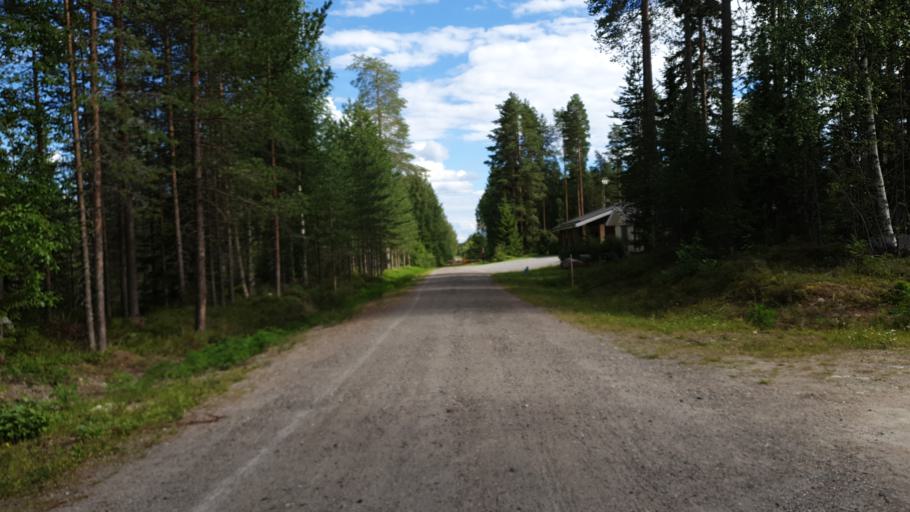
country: FI
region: Kainuu
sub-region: Kehys-Kainuu
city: Kuhmo
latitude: 64.1148
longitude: 29.5171
